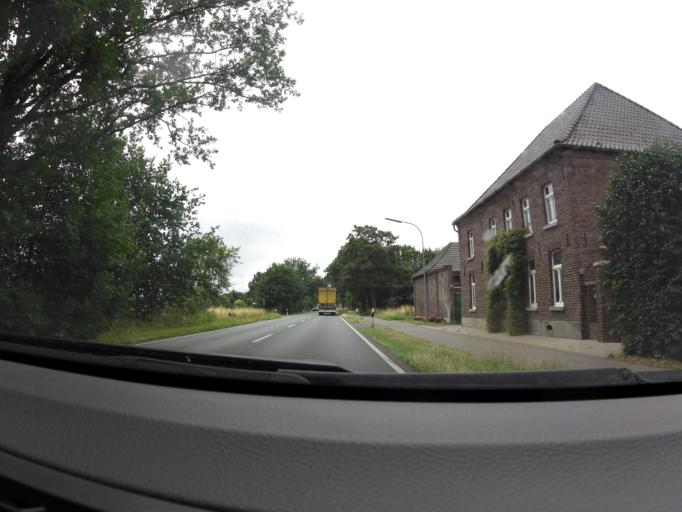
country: DE
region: North Rhine-Westphalia
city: Straelen
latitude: 51.4595
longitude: 6.2771
